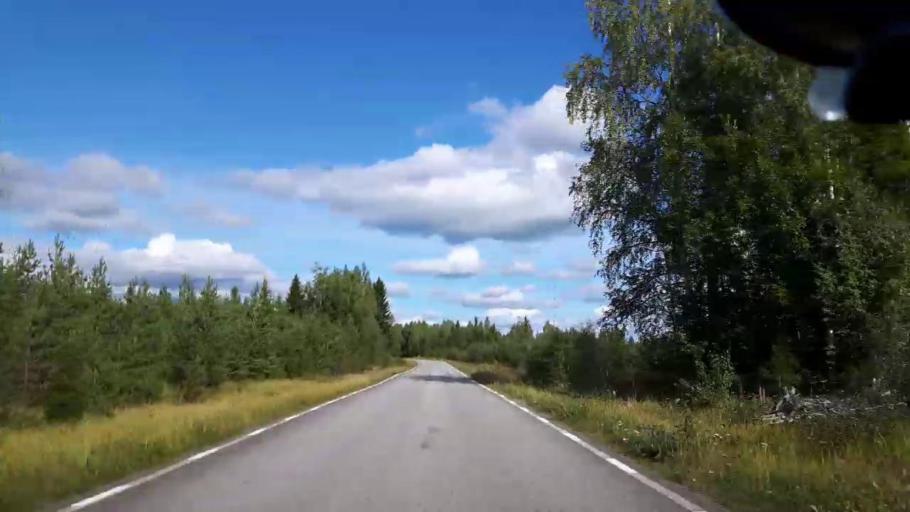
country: SE
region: Jaemtland
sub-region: OEstersunds Kommun
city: Brunflo
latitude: 63.2087
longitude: 15.2483
